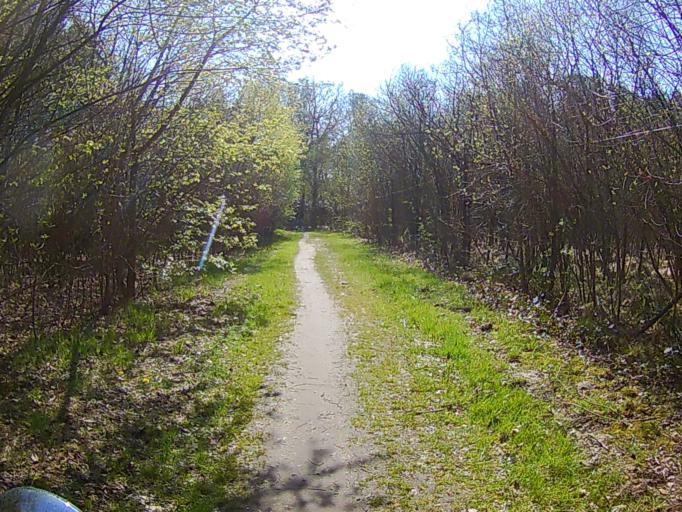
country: BE
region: Flanders
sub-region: Provincie Antwerpen
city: Schoten
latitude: 51.2822
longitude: 4.5380
